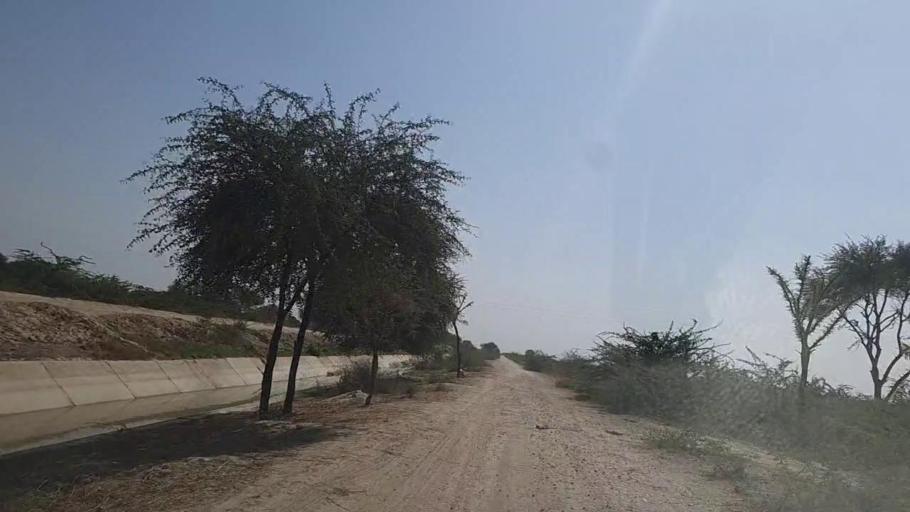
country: PK
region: Sindh
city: Naukot
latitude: 24.6508
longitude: 69.2768
